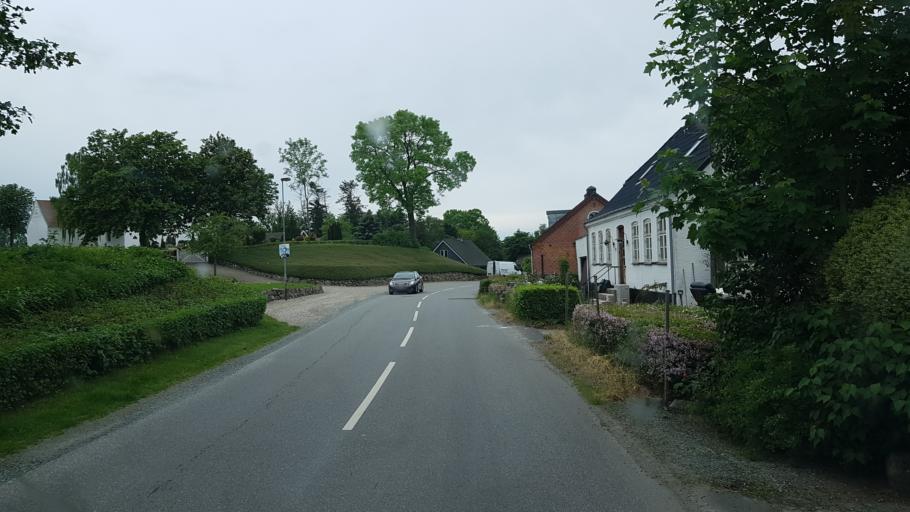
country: DK
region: South Denmark
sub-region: Middelfart Kommune
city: Brenderup
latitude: 55.4414
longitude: 10.0148
